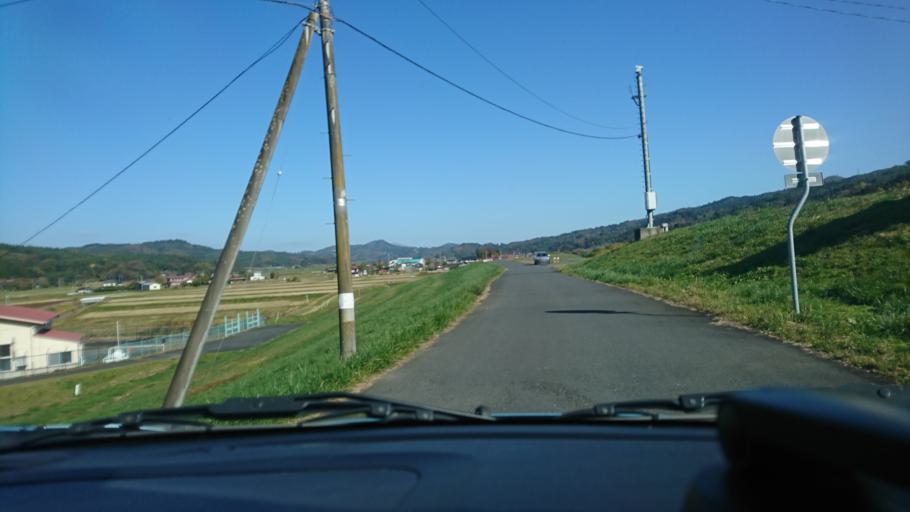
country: JP
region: Iwate
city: Ichinoseki
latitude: 38.8280
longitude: 141.2495
